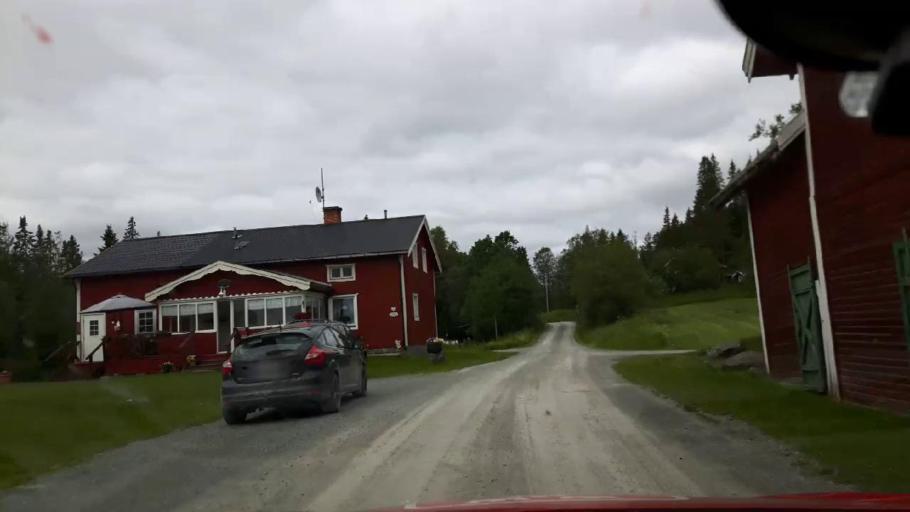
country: SE
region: Jaemtland
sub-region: OEstersunds Kommun
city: Brunflo
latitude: 63.0325
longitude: 14.9332
